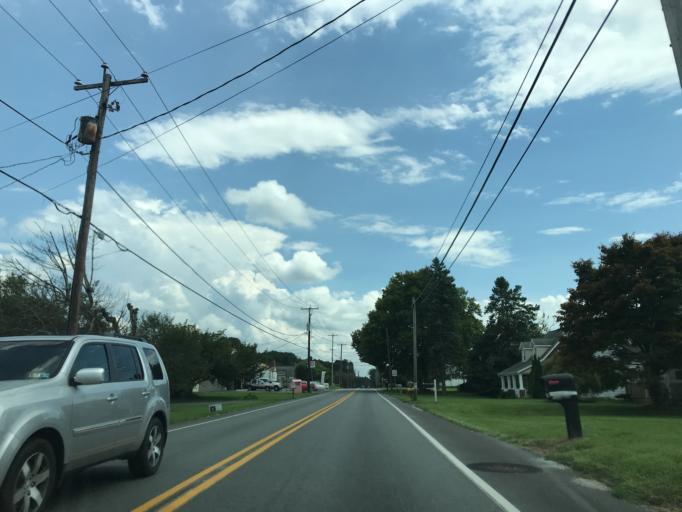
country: US
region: Pennsylvania
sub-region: York County
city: Windsor
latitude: 39.8906
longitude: -76.5556
